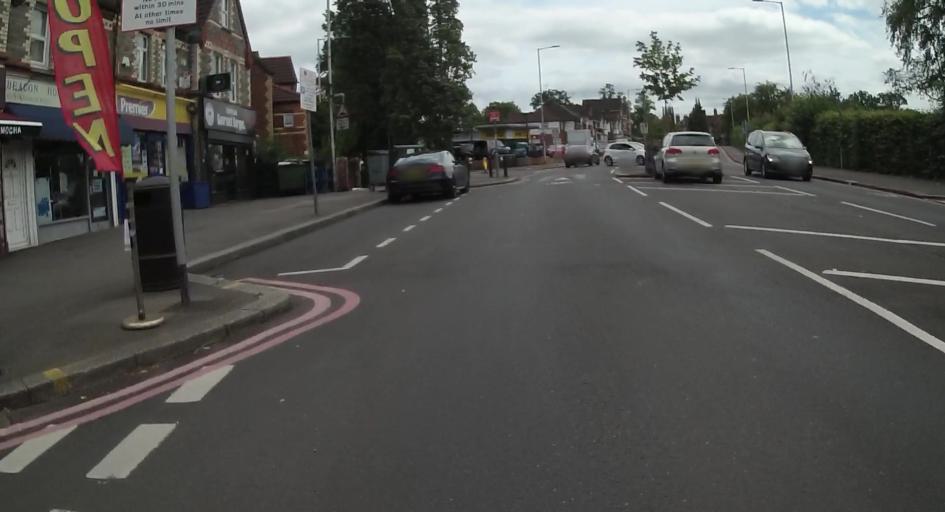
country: GB
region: England
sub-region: Wokingham
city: Earley
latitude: 51.4480
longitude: -0.9363
